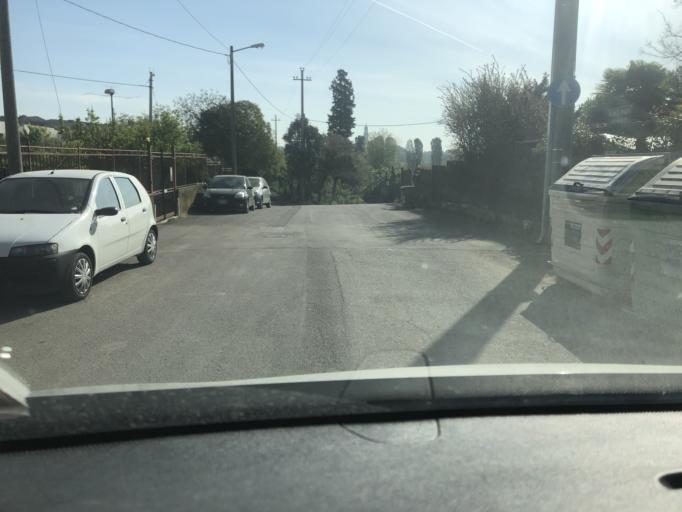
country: IT
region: Veneto
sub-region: Provincia di Verona
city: Poiano
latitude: 45.4342
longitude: 11.0272
